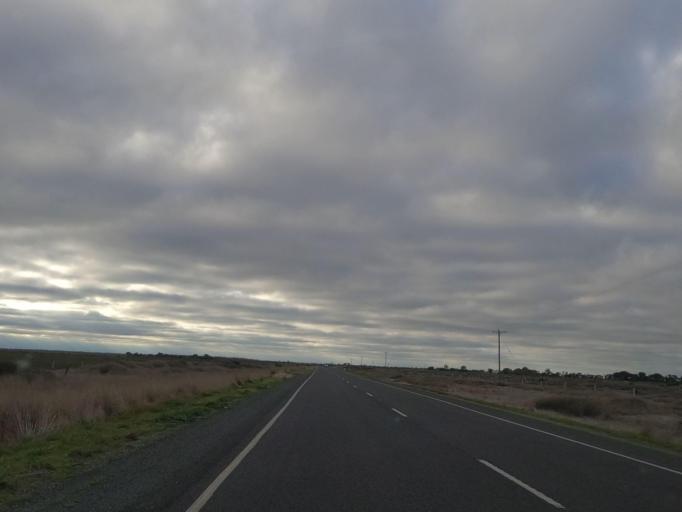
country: AU
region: Victoria
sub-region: Swan Hill
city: Swan Hill
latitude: -35.8469
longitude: 143.9379
